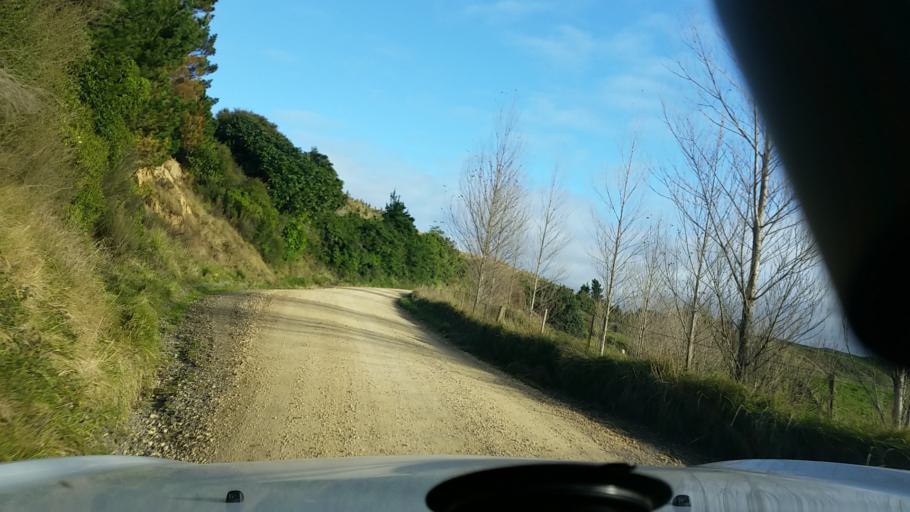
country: NZ
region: Hawke's Bay
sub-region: Napier City
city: Napier
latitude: -39.2612
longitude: 176.8509
